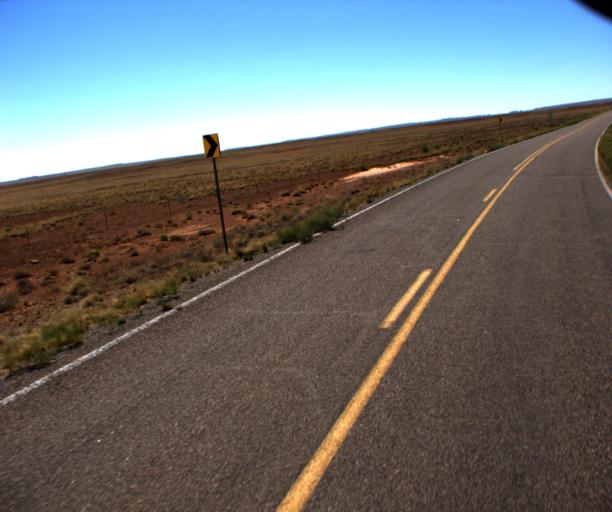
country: US
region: Arizona
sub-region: Coconino County
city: LeChee
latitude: 35.1728
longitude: -110.9192
